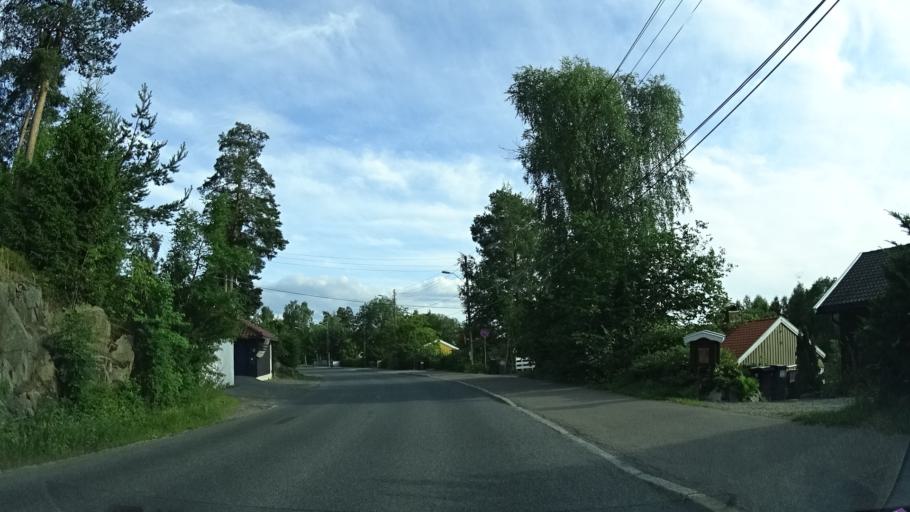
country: NO
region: Oslo
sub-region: Oslo
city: Sjolyststranda
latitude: 59.9587
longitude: 10.6512
